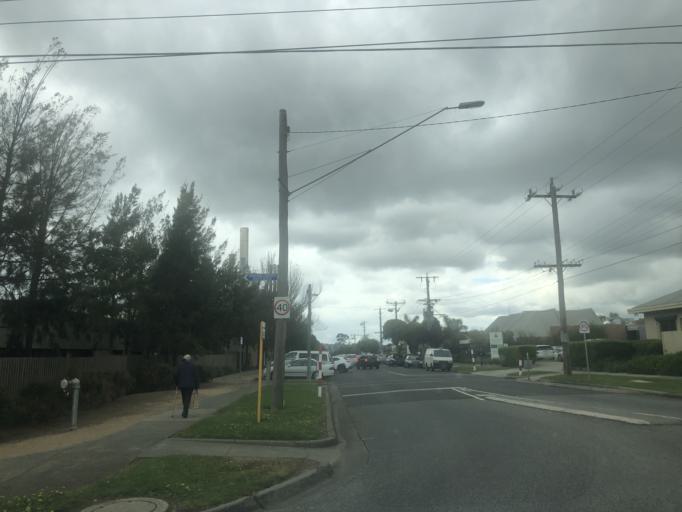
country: AU
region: Victoria
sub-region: Greater Dandenong
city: Dandenong North
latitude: -37.9769
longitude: 145.2161
